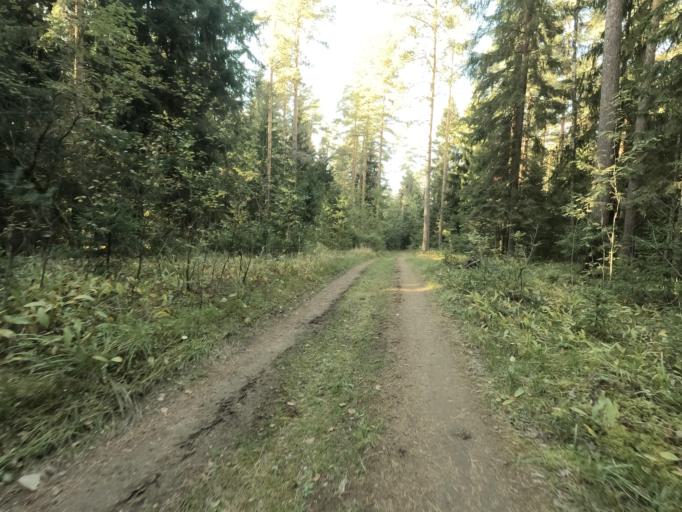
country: RU
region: Leningrad
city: Imeni Sverdlova
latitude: 59.8410
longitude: 30.7300
